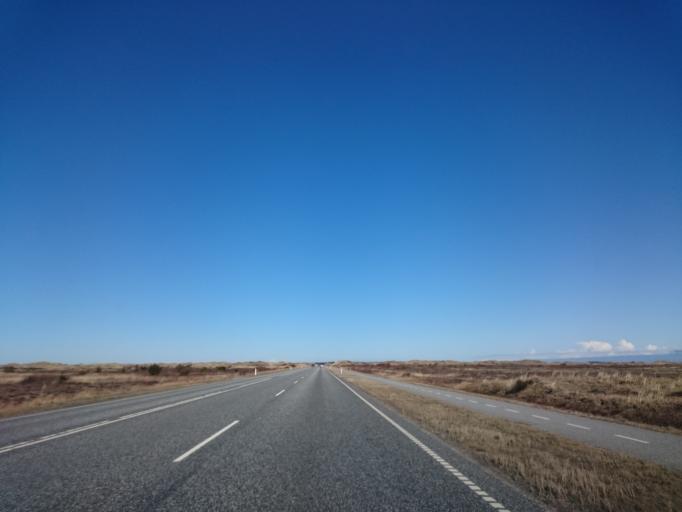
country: DK
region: North Denmark
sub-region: Frederikshavn Kommune
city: Skagen
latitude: 57.6780
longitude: 10.4604
